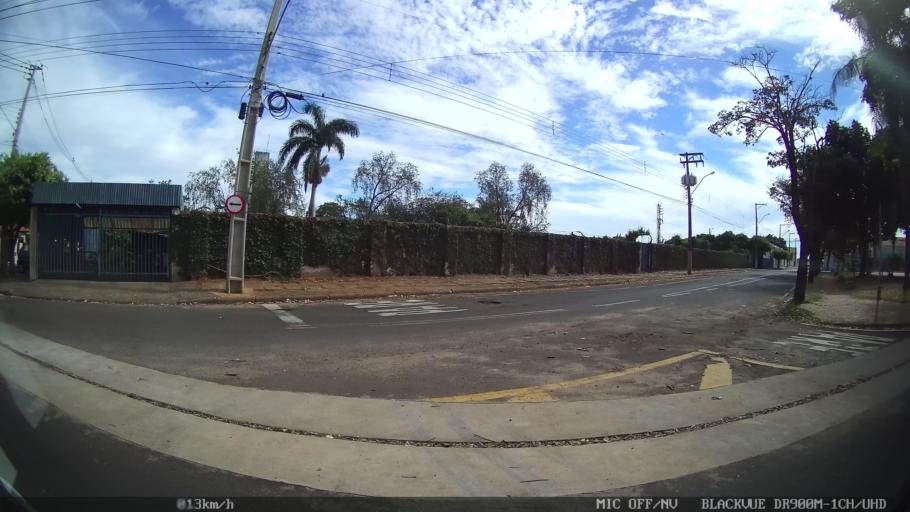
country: BR
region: Sao Paulo
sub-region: Catanduva
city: Catanduva
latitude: -21.1319
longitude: -48.9572
